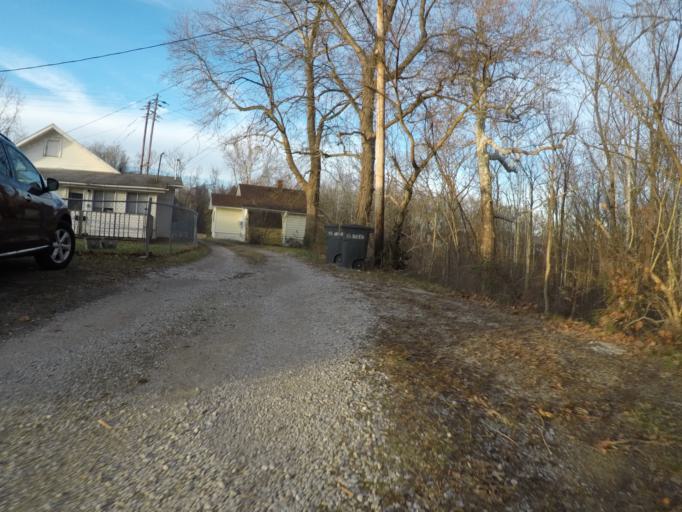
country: US
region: Ohio
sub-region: Lawrence County
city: Burlington
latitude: 38.4042
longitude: -82.4986
